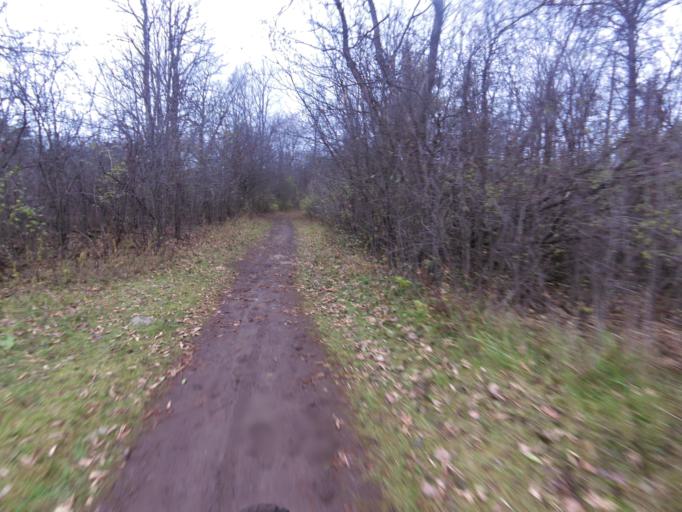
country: CA
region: Ontario
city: Bells Corners
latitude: 45.2817
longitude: -75.8320
